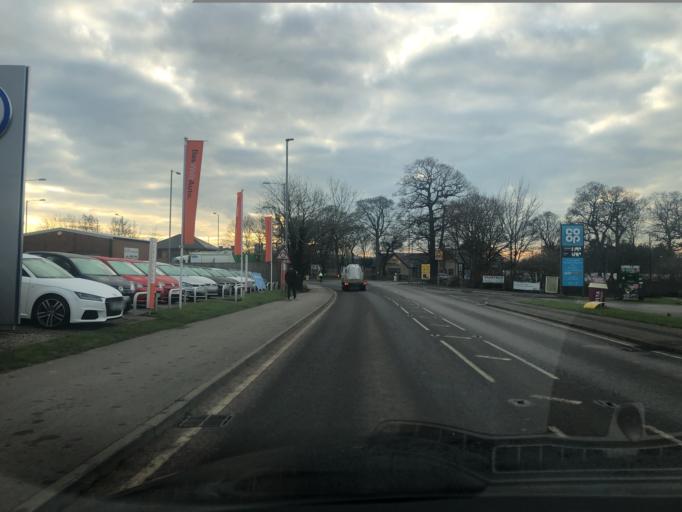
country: GB
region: England
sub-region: North Yorkshire
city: Northallerton
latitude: 54.3470
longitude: -1.4412
